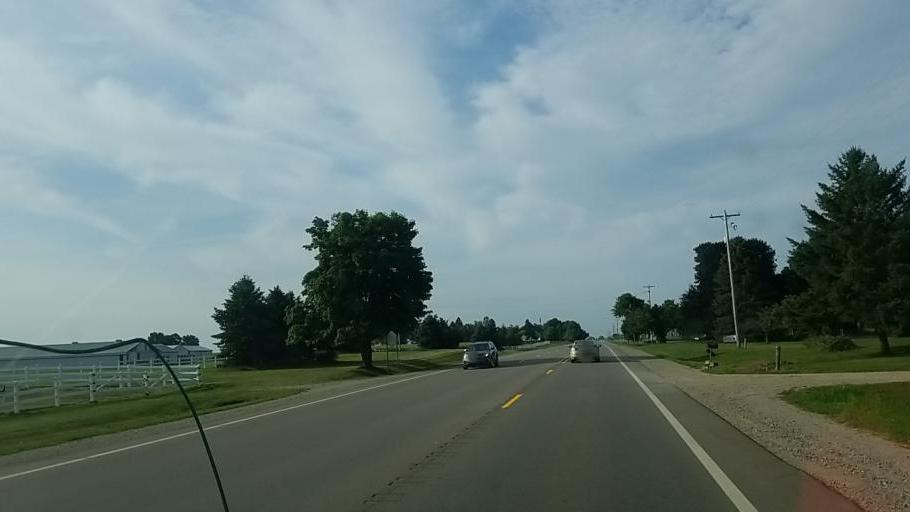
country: US
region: Michigan
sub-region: Ionia County
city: Ionia
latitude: 42.8937
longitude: -85.0750
